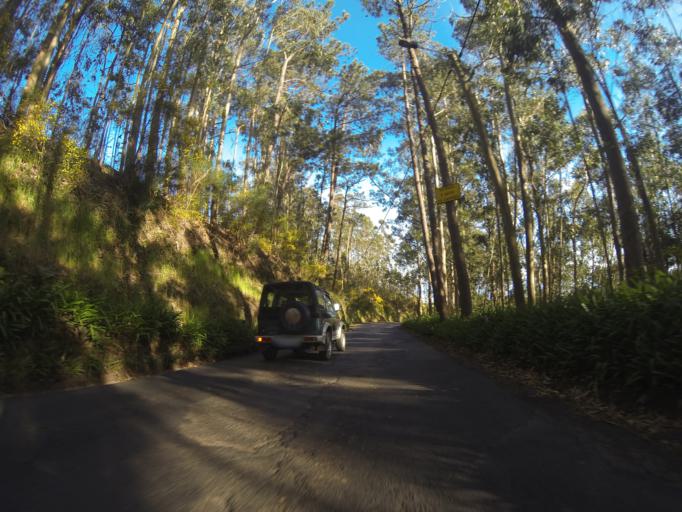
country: PT
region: Madeira
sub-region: Santa Cruz
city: Camacha
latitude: 32.6890
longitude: -16.8755
